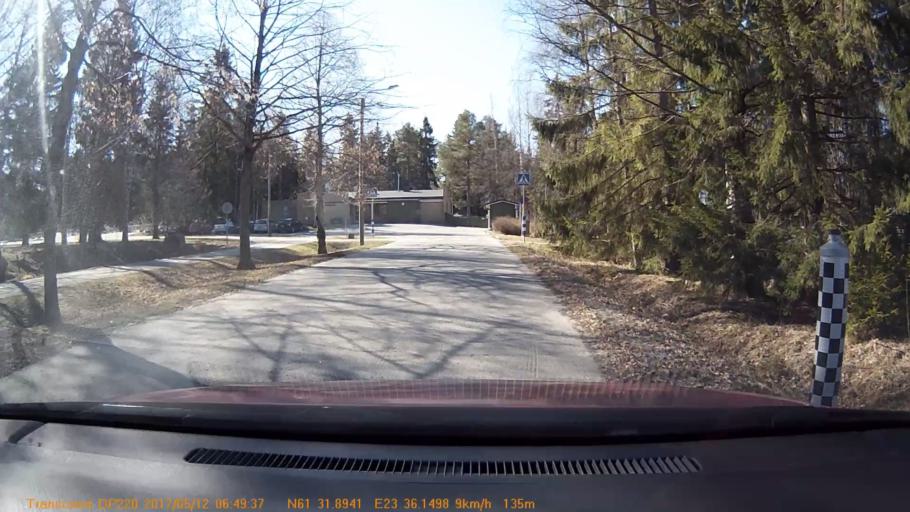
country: FI
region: Pirkanmaa
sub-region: Tampere
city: Yloejaervi
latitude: 61.5316
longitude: 23.6025
